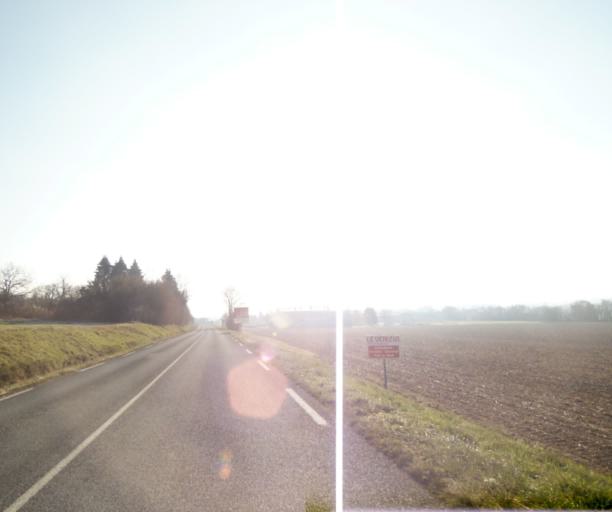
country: FR
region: Champagne-Ardenne
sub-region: Departement de la Haute-Marne
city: Wassy
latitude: 48.5081
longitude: 4.9408
